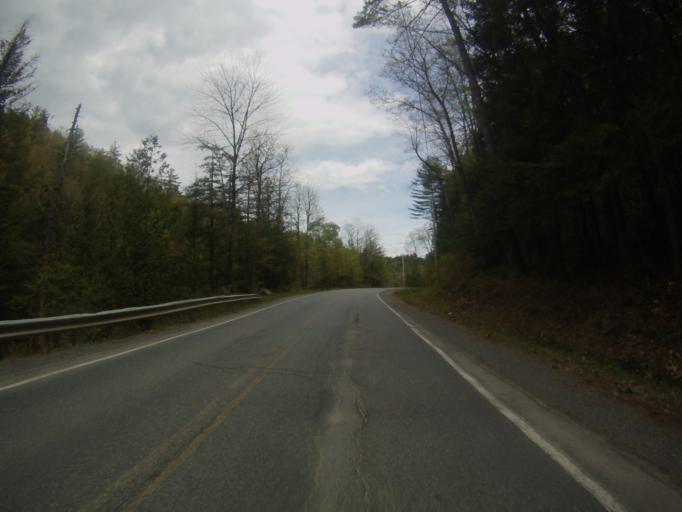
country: US
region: New York
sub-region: Essex County
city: Port Henry
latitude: 43.9463
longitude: -73.4926
